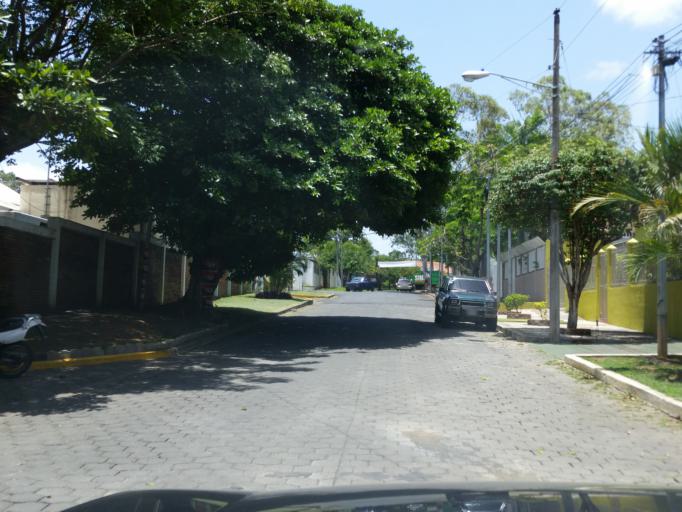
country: NI
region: Managua
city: Managua
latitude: 12.1144
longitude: -86.2789
